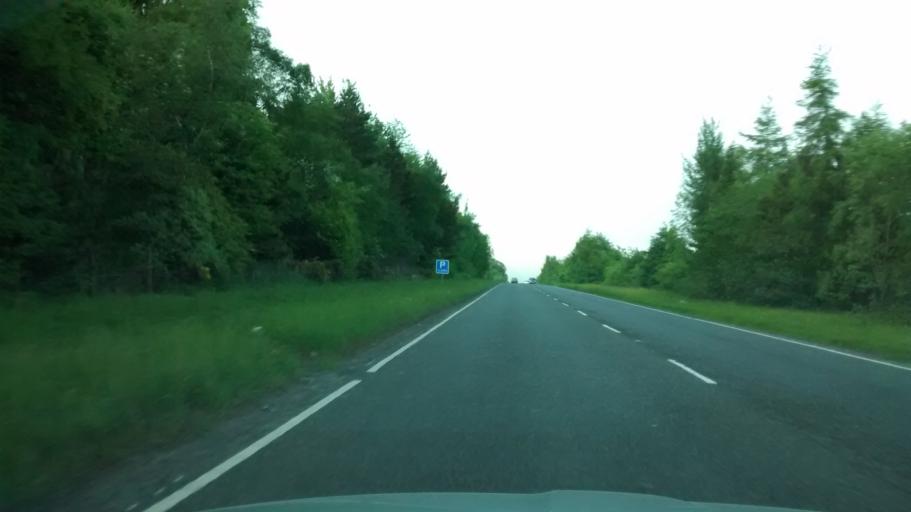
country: GB
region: Scotland
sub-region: West Lothian
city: Whitburn
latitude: 55.8738
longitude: -3.6794
